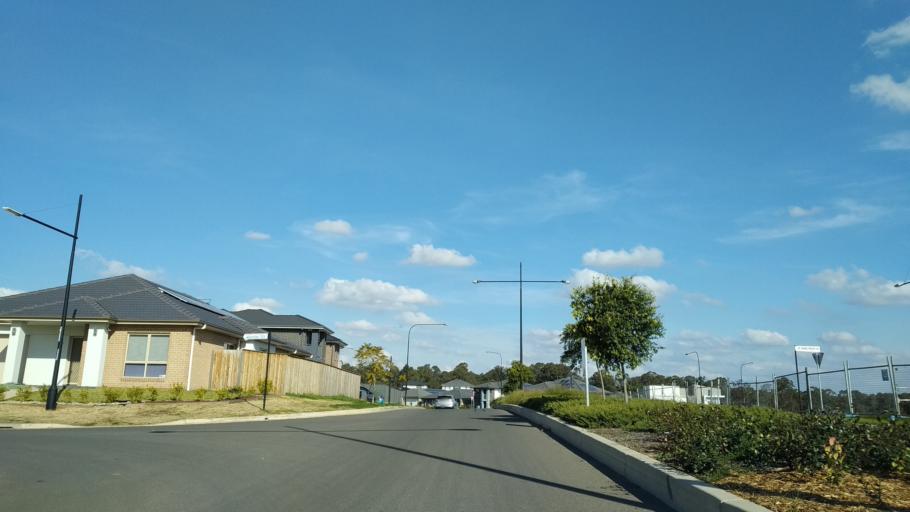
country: AU
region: New South Wales
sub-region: Blacktown
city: Hassall Grove
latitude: -33.7214
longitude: 150.8533
